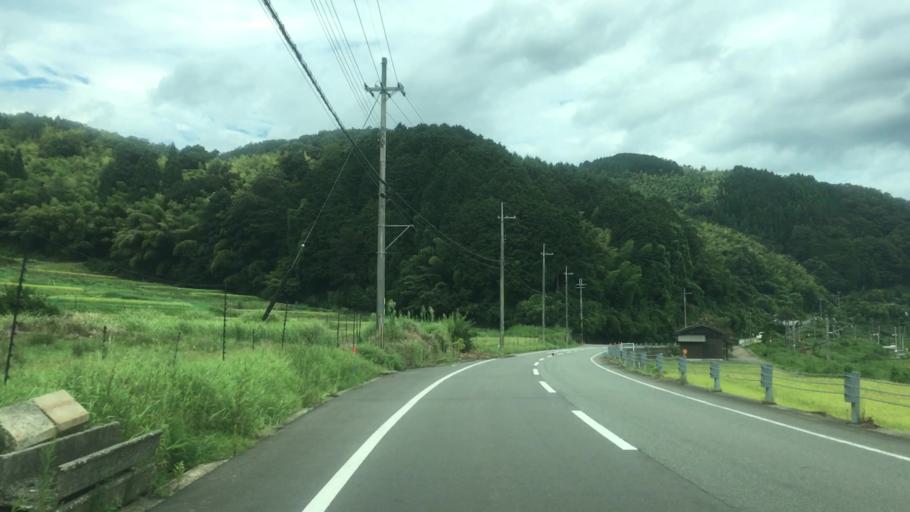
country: JP
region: Hyogo
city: Toyooka
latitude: 35.5780
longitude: 134.8009
